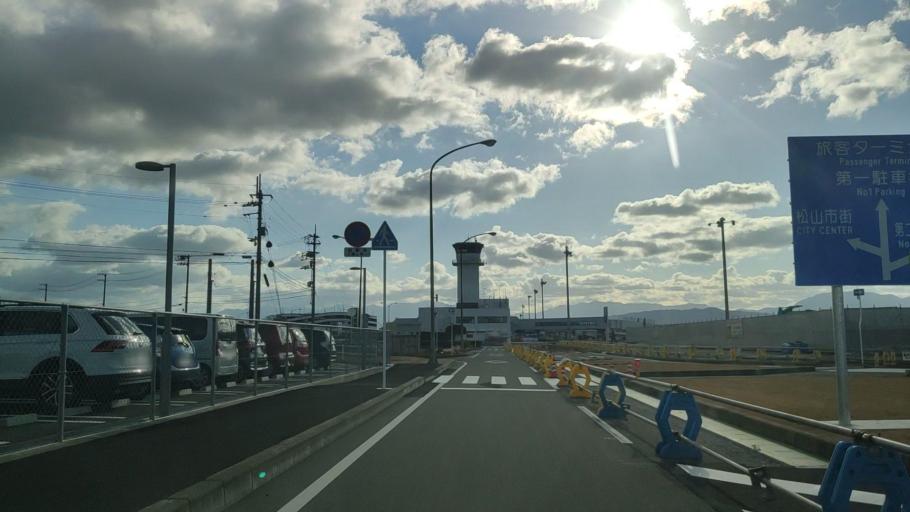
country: JP
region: Ehime
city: Masaki-cho
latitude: 33.8310
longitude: 132.7009
